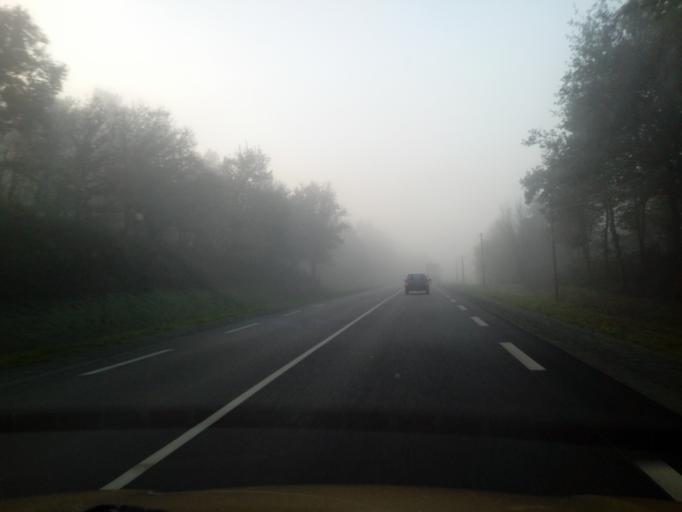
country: FR
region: Brittany
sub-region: Departement du Morbihan
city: Mauron
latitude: 48.0482
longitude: -2.3018
